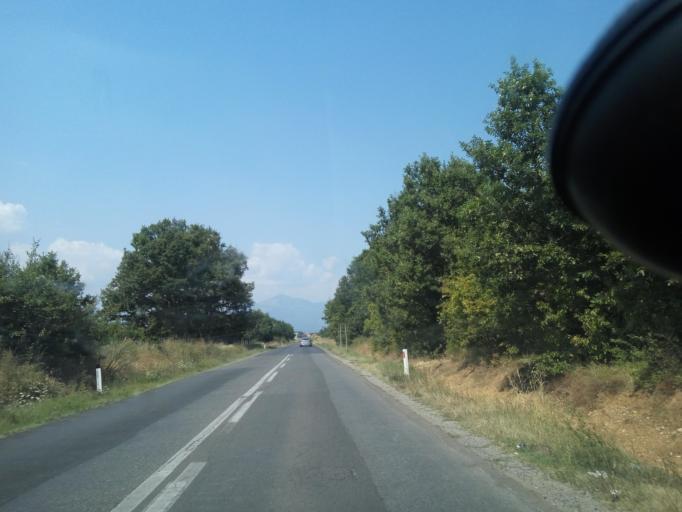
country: XK
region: Gjakova
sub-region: Komuna e Decanit
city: Gllogjan
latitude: 42.4399
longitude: 20.3685
